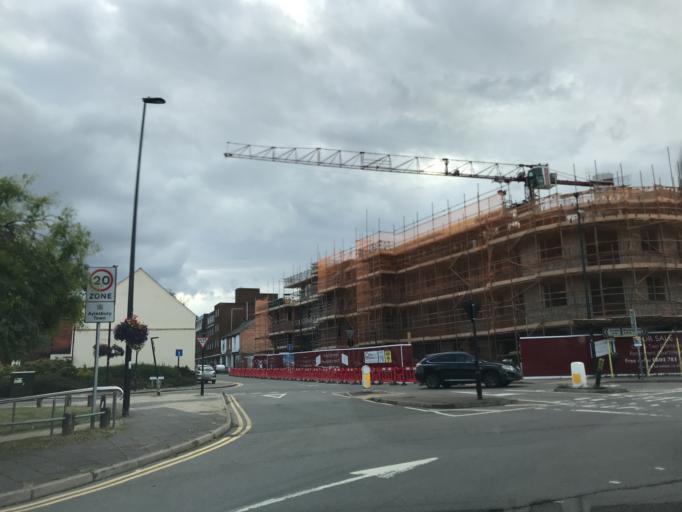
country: GB
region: England
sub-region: Buckinghamshire
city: Aylesbury
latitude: 51.8184
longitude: -0.8105
